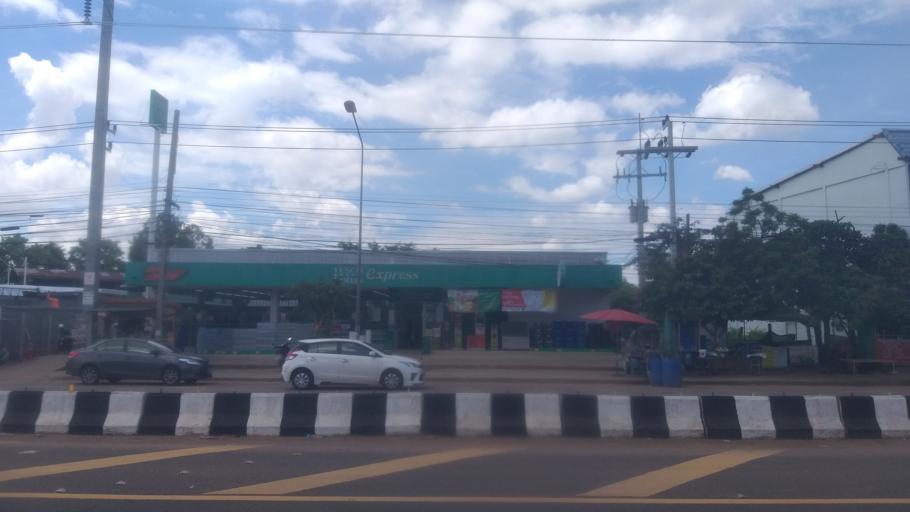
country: TH
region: Nakhon Ratchasima
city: Phra Thong Kham
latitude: 15.3099
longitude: 101.9672
